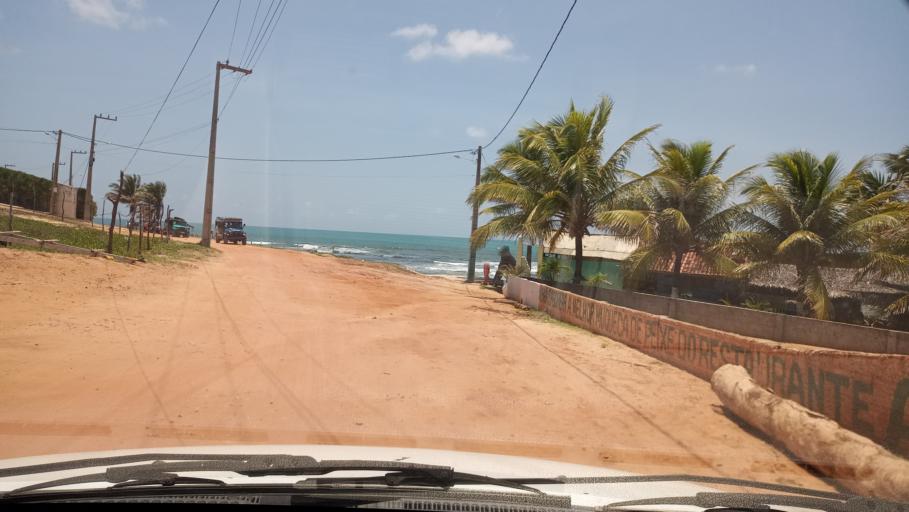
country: BR
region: Rio Grande do Norte
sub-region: Canguaretama
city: Canguaretama
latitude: -6.2782
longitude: -35.0354
